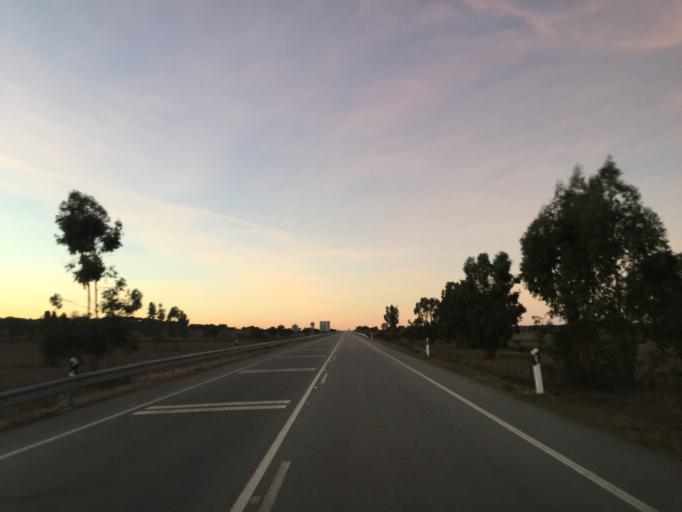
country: PT
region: Portalegre
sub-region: Alter do Chao
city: Alter do Chao
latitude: 39.2965
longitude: -7.6310
